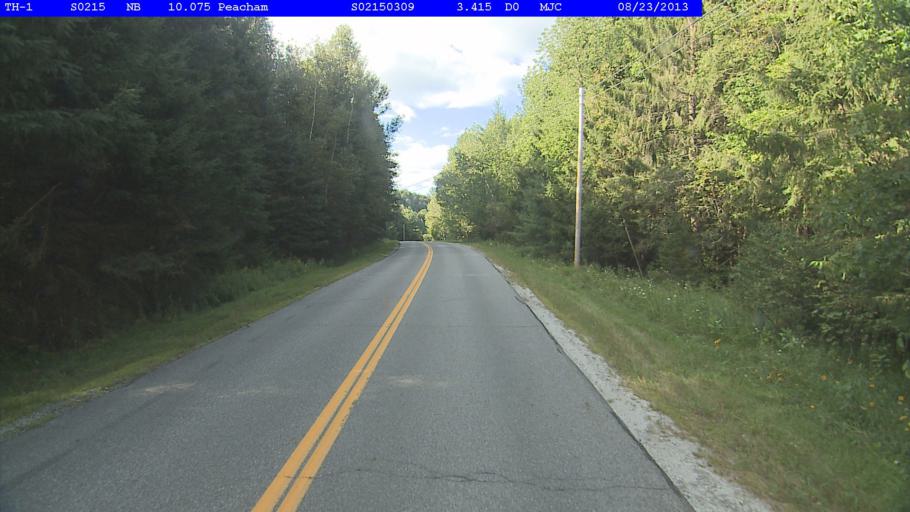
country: US
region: Vermont
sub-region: Caledonia County
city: Saint Johnsbury
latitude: 44.3456
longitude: -72.1768
